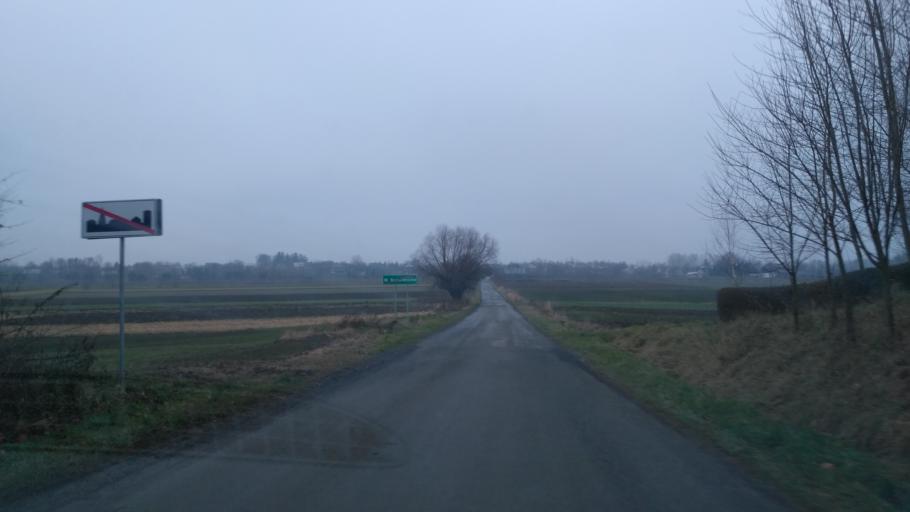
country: PL
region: Subcarpathian Voivodeship
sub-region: Powiat przeworski
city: Zarzecze
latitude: 49.9712
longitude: 22.5657
